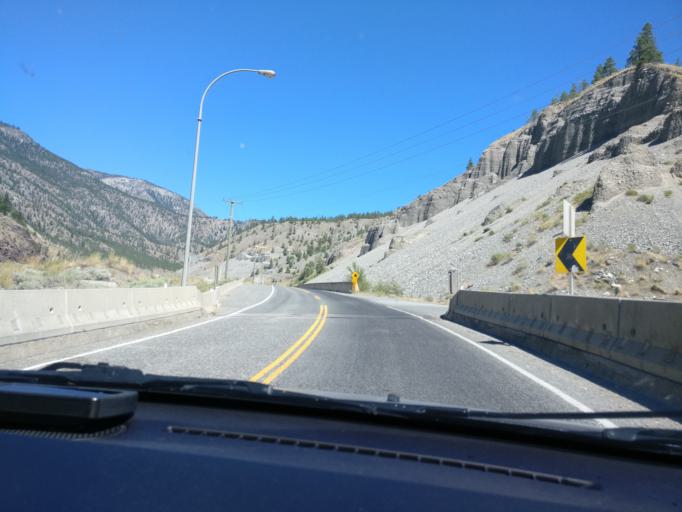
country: CA
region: British Columbia
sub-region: Thompson-Nicola Regional District
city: Ashcroft
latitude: 50.2688
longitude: -121.4011
